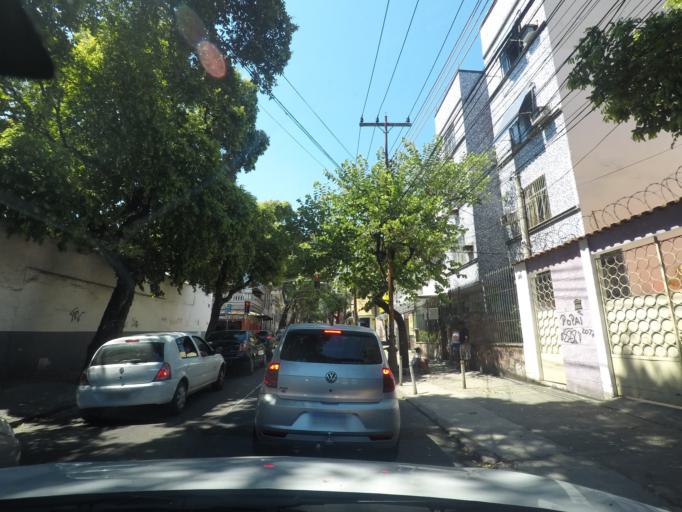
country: BR
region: Rio de Janeiro
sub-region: Rio De Janeiro
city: Rio de Janeiro
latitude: -22.9151
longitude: -43.2505
